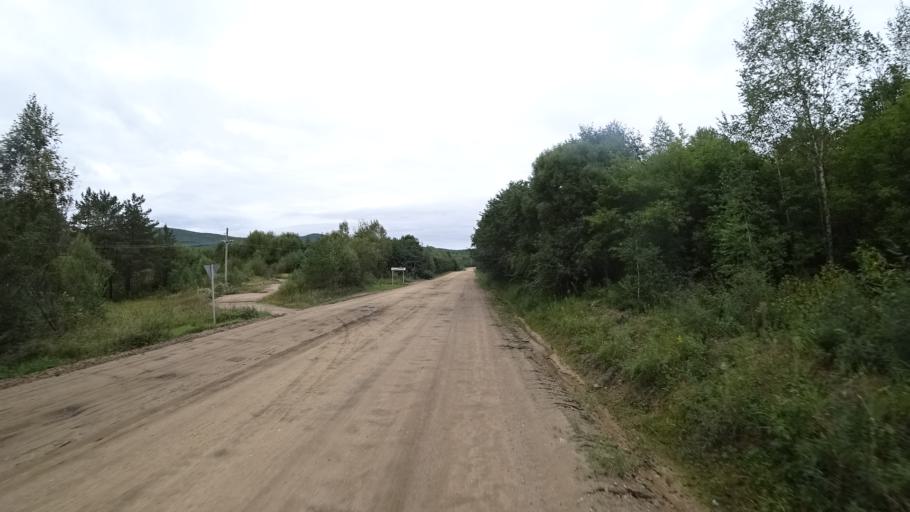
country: RU
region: Primorskiy
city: Rettikhovka
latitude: 44.1708
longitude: 132.7943
